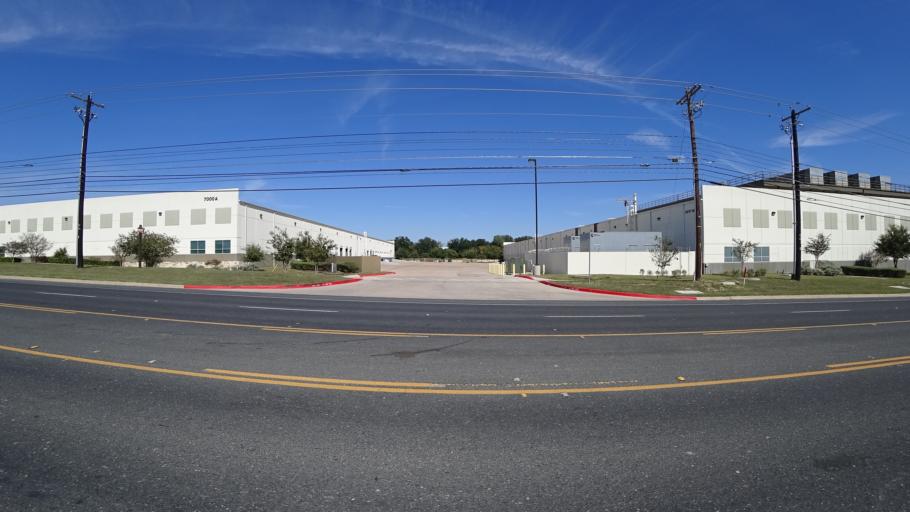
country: US
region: Texas
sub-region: Travis County
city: Austin
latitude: 30.2004
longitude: -97.7083
